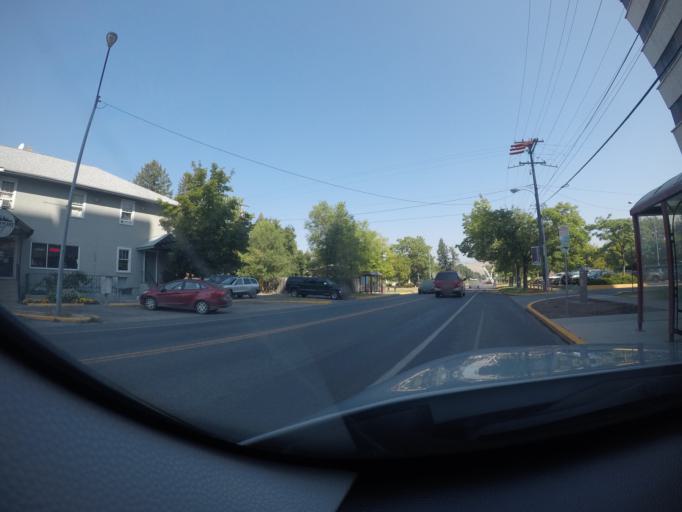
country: US
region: Montana
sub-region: Missoula County
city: Missoula
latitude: 46.8614
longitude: -113.9892
